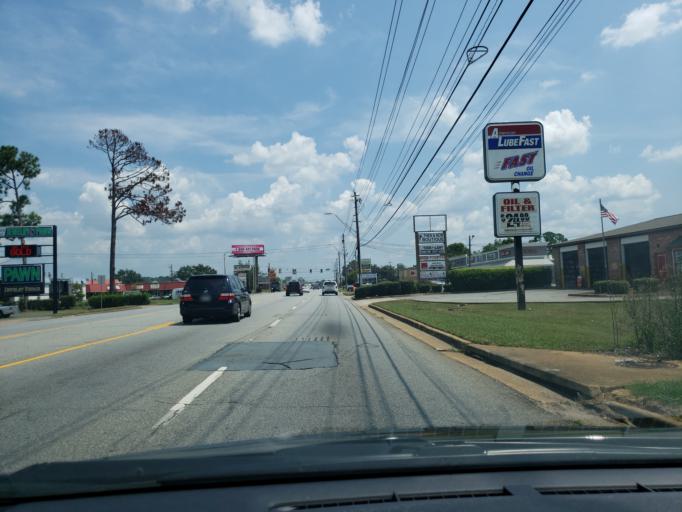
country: US
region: Georgia
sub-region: Dougherty County
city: Albany
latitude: 31.6102
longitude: -84.2115
